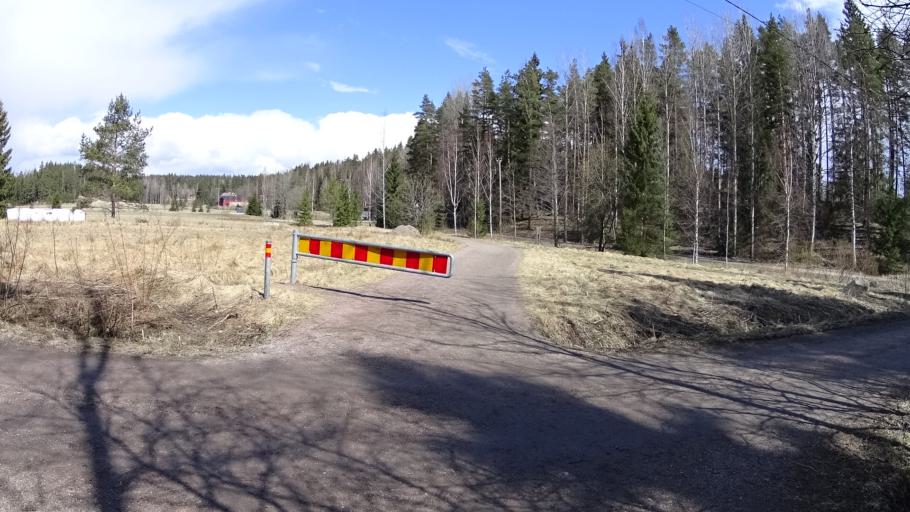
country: FI
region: Uusimaa
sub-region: Helsinki
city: Espoo
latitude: 60.2687
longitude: 24.6474
